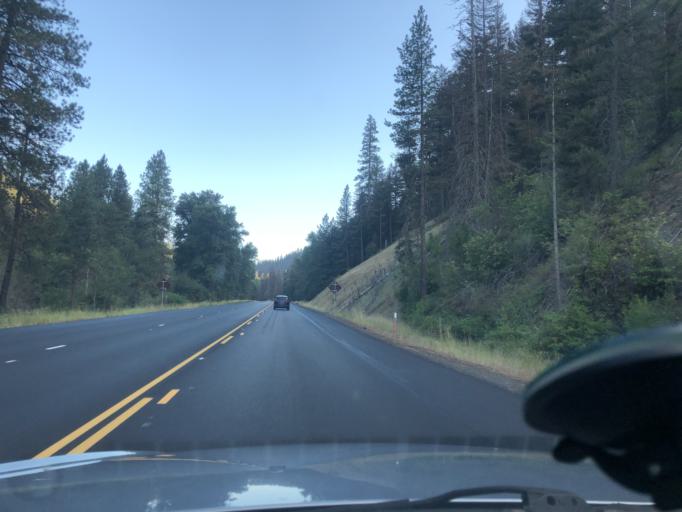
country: US
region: Washington
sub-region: Kittitas County
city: Cle Elum
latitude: 47.2699
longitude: -120.6980
